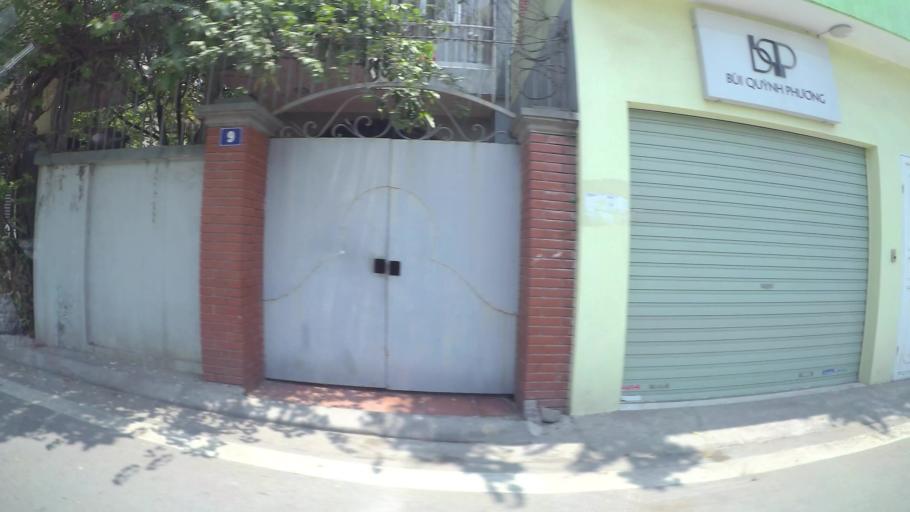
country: VN
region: Ha Noi
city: Hoan Kiem
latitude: 21.0278
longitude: 105.8826
